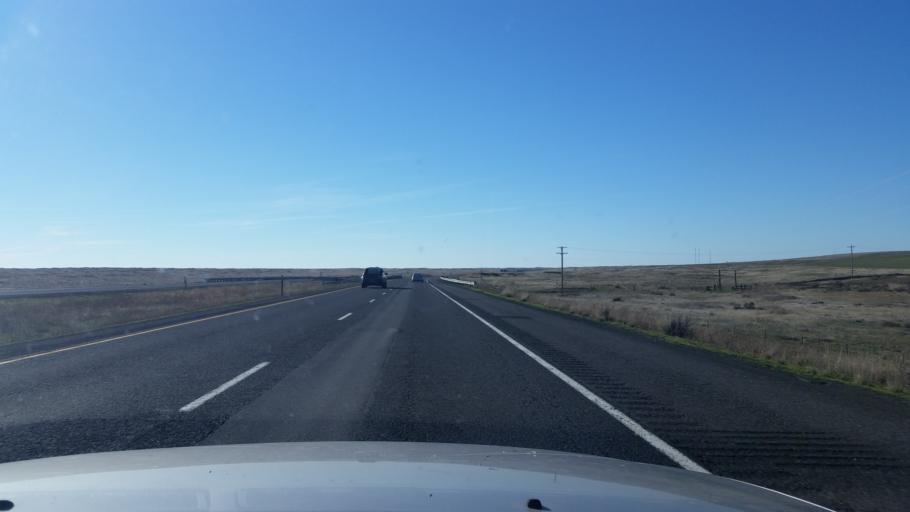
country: US
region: Washington
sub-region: Spokane County
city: Medical Lake
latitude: 47.3422
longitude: -117.9068
